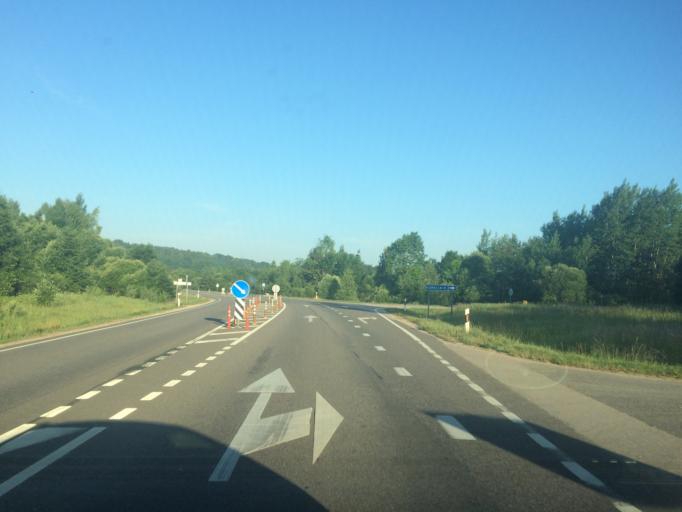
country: LT
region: Utenos apskritis
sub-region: Anyksciai
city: Anyksciai
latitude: 55.4059
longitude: 25.1118
